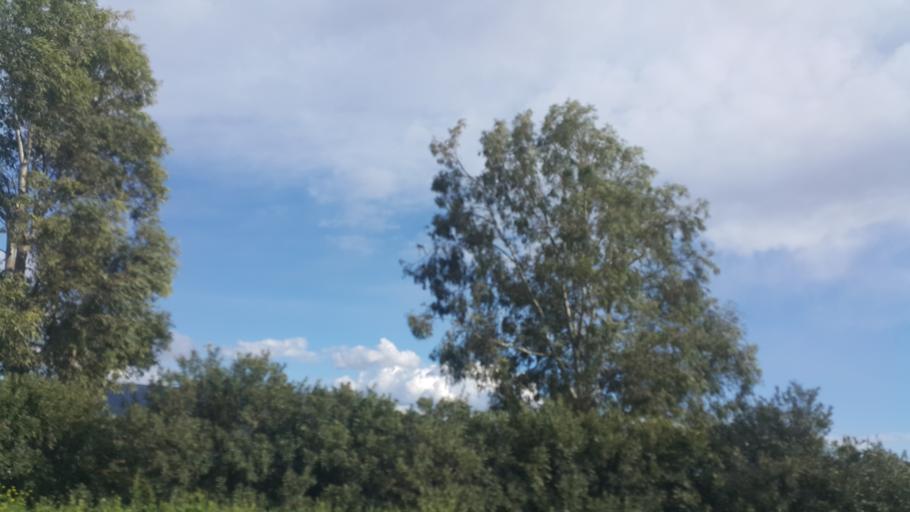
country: TR
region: Adana
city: Yakapinar
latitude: 37.0048
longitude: 35.6680
